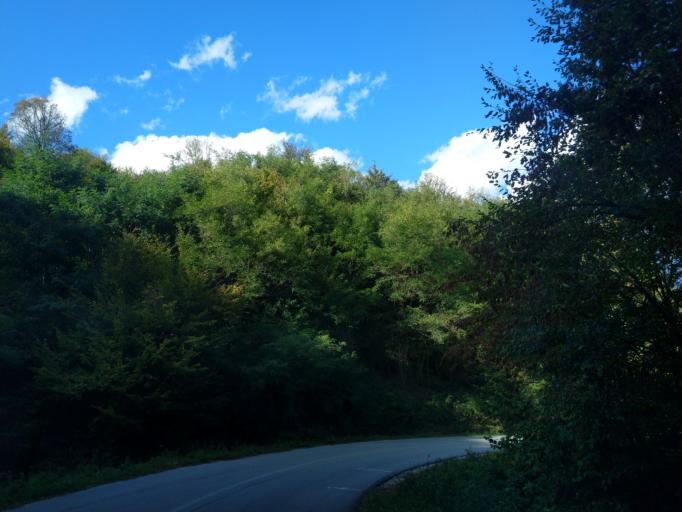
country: RS
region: Central Serbia
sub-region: Zlatiborski Okrug
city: Uzice
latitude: 43.8838
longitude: 19.7754
